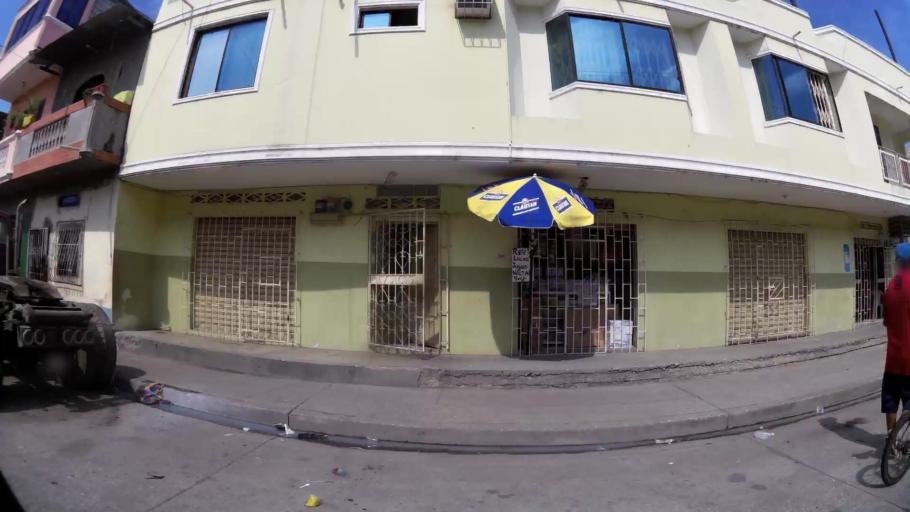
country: EC
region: Guayas
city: Guayaquil
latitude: -2.2789
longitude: -79.8827
